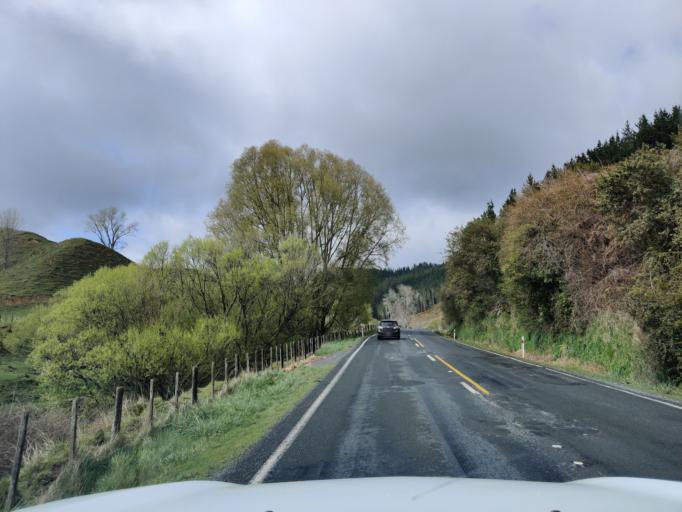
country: NZ
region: Waikato
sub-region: Otorohanga District
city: Otorohanga
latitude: -38.6121
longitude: 175.2185
